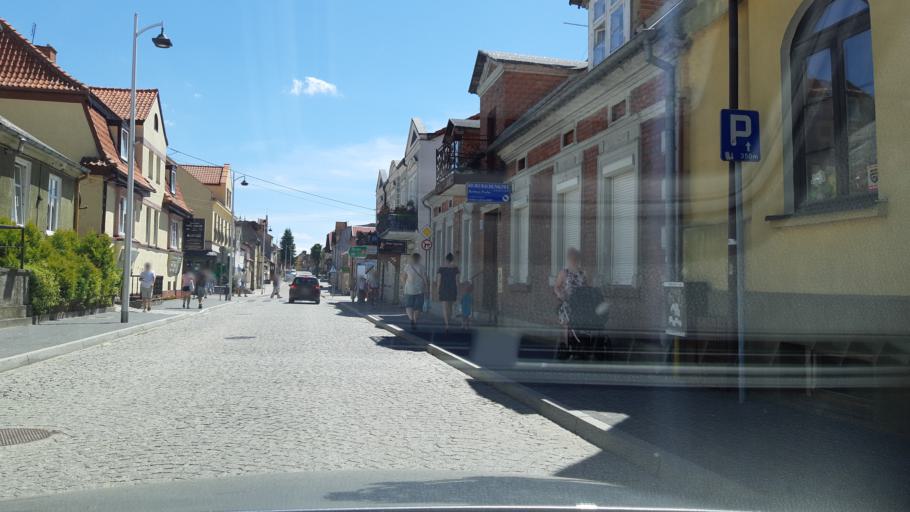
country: PL
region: Warmian-Masurian Voivodeship
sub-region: Powiat mragowski
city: Mikolajki
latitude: 53.8002
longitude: 21.5735
